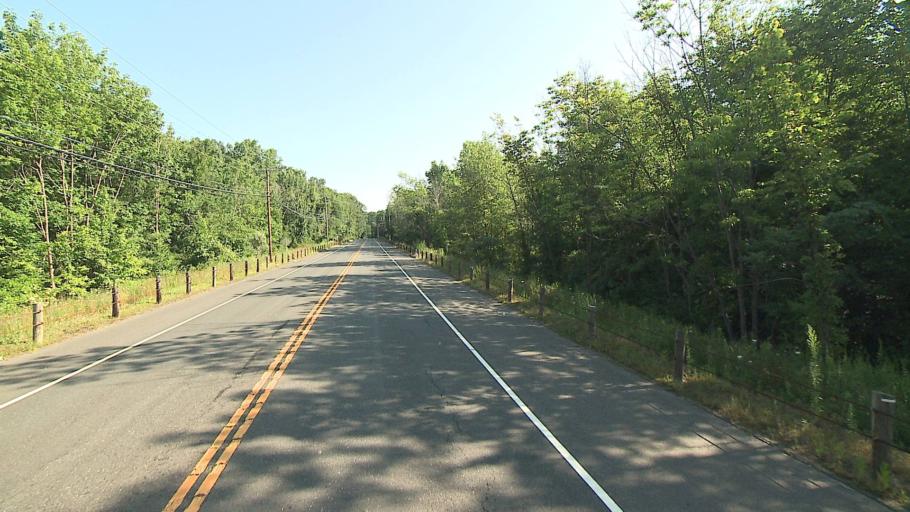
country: US
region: Connecticut
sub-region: Litchfield County
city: Northwest Harwinton
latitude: 41.7754
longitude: -73.0693
